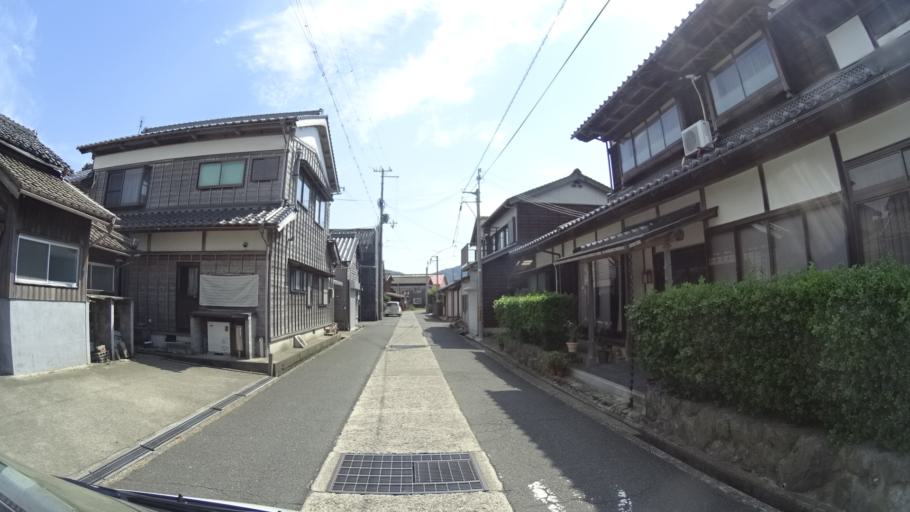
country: JP
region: Kyoto
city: Miyazu
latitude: 35.6879
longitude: 135.0292
